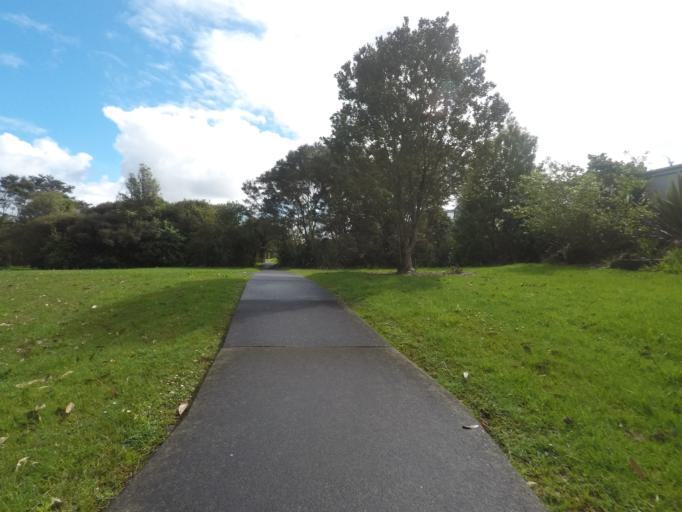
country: NZ
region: Auckland
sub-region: Auckland
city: Rosebank
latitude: -36.9030
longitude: 174.7000
